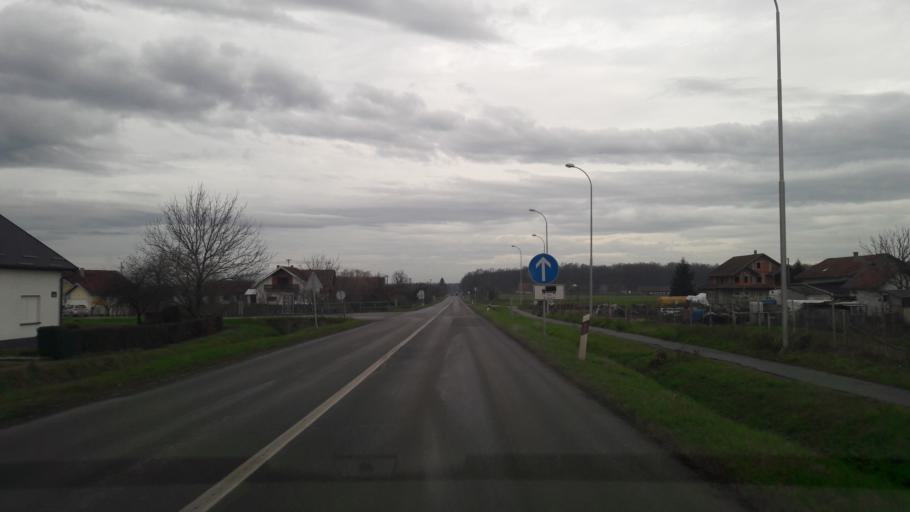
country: HR
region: Osjecko-Baranjska
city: Velimirovac
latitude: 45.5258
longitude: 18.0966
